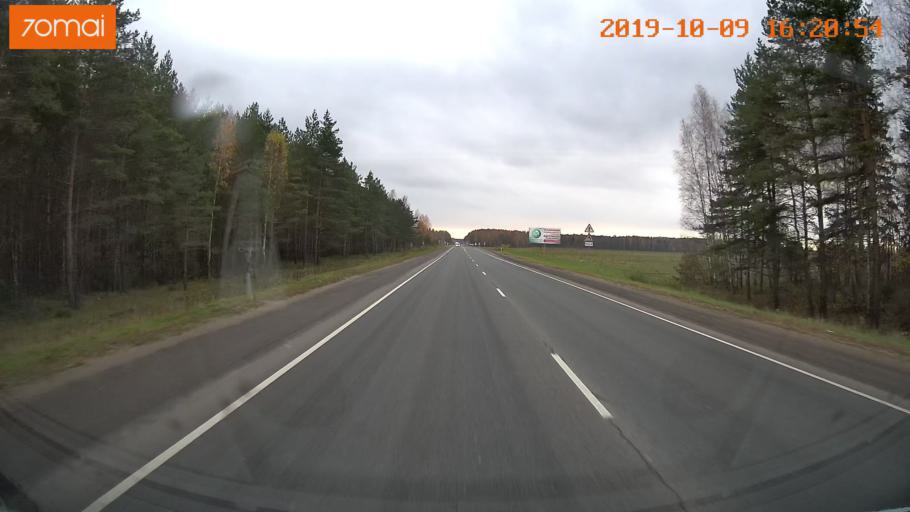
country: RU
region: Kostroma
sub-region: Kostromskoy Rayon
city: Kostroma
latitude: 57.7004
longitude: 40.8909
